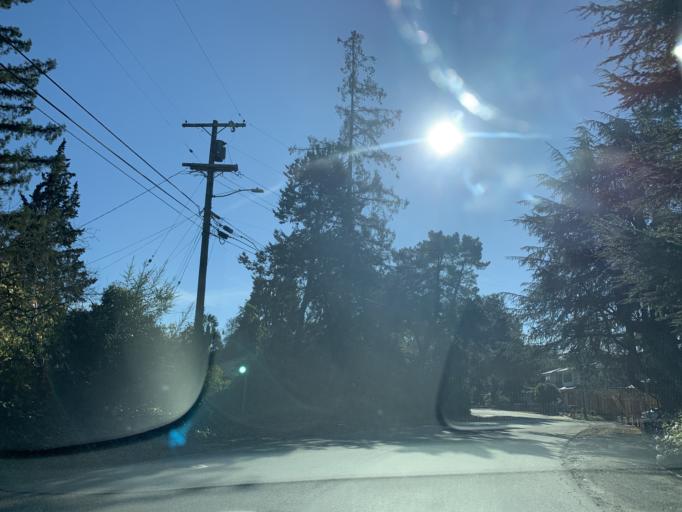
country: US
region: California
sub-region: Santa Clara County
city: Los Altos
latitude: 37.3861
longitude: -122.1054
